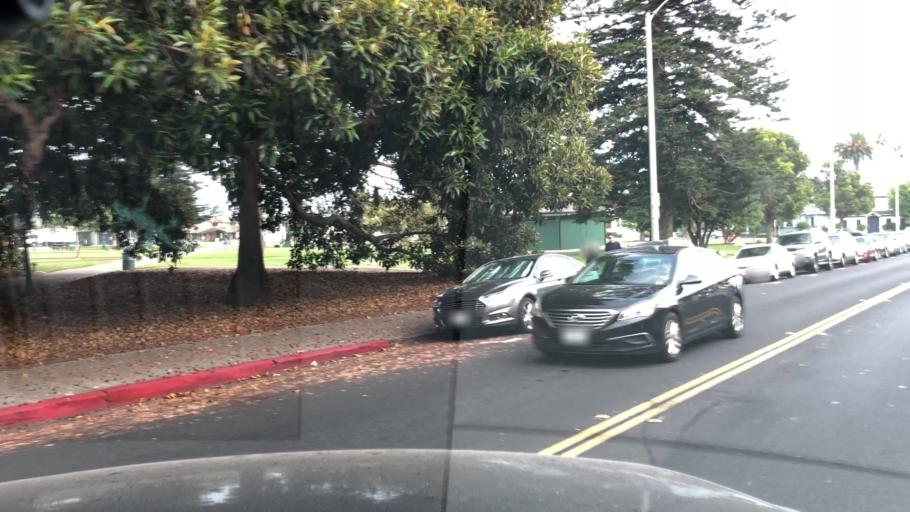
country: US
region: California
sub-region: Ventura County
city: Ventura
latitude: 34.2795
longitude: -119.2916
